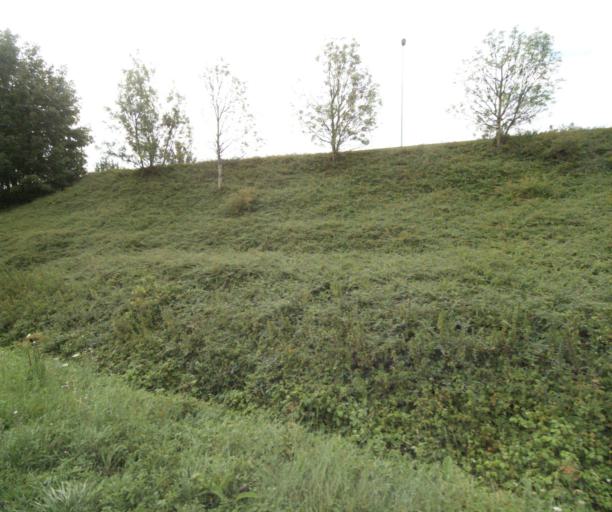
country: FR
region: Nord-Pas-de-Calais
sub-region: Departement du Nord
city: Hem
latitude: 50.6506
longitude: 3.1689
